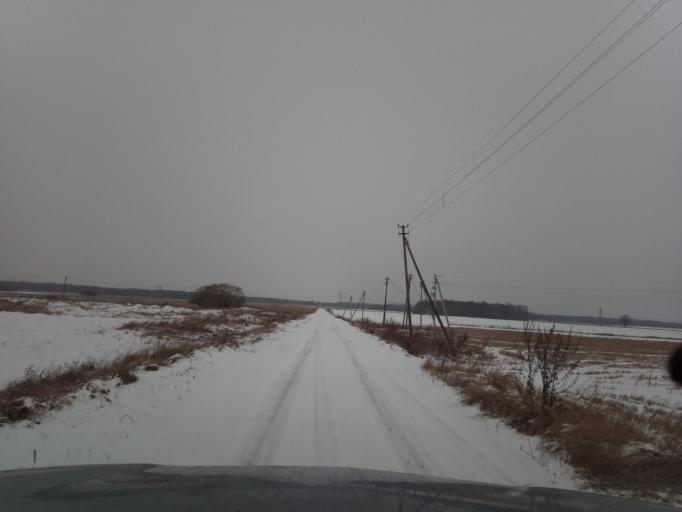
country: LT
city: Ramygala
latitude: 55.6189
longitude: 24.3434
